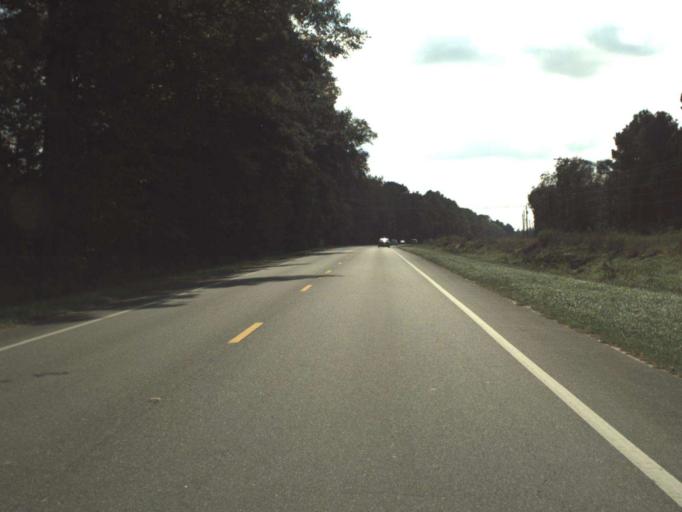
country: US
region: Florida
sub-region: Holmes County
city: Bonifay
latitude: 30.6431
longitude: -85.7014
